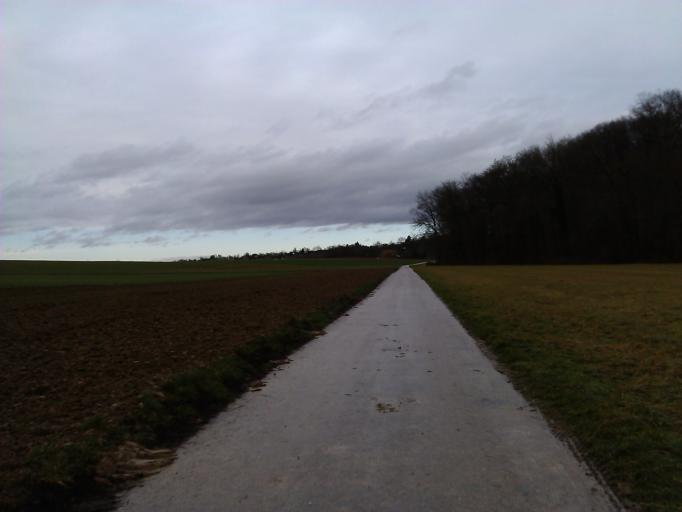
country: DE
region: Baden-Wuerttemberg
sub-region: Regierungsbezirk Stuttgart
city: Bad Wimpfen
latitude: 49.2072
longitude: 9.1591
